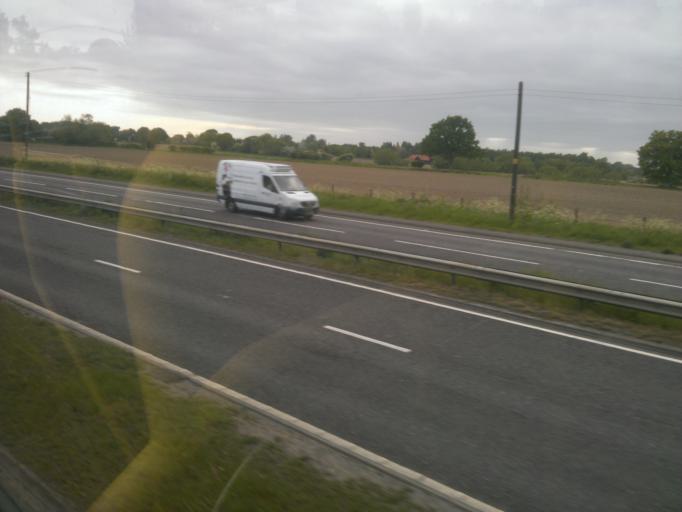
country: GB
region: England
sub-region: Suffolk
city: East Bergholt
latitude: 51.9518
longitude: 0.9614
